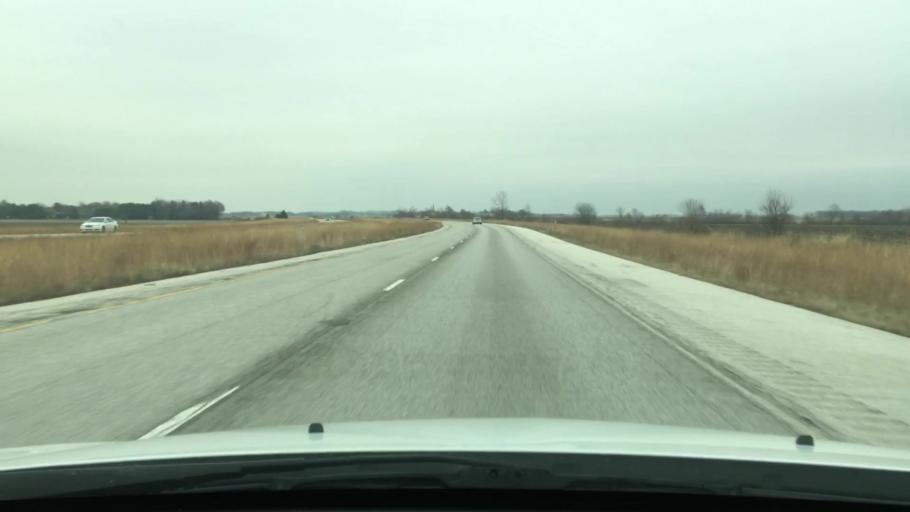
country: US
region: Illinois
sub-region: Morgan County
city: South Jacksonville
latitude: 39.6864
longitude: -90.2134
